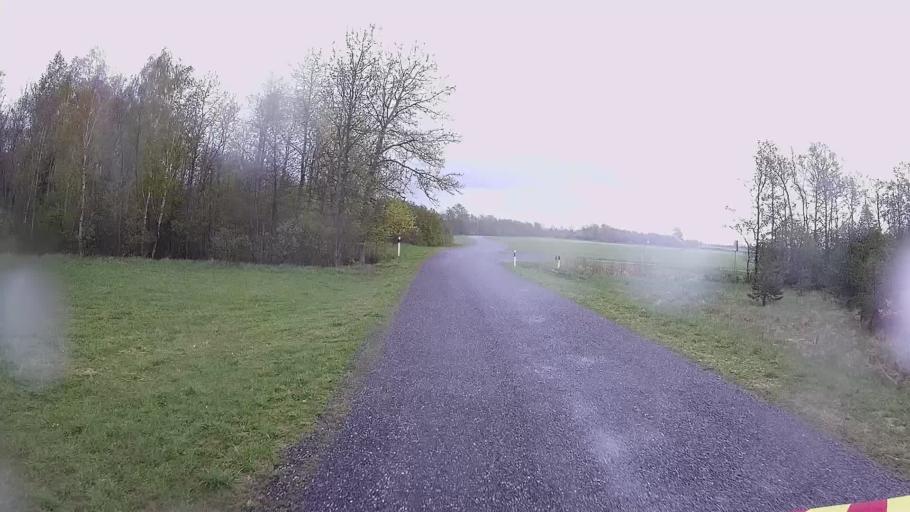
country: EE
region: Hiiumaa
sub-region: Kaerdla linn
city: Kardla
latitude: 58.6962
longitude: 22.5532
